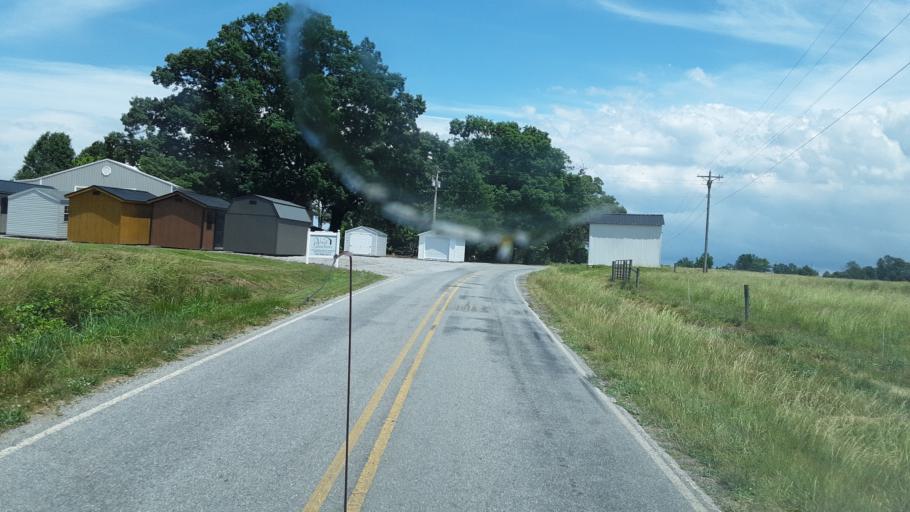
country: US
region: North Carolina
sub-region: Yadkin County
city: Yadkinville
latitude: 36.0683
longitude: -80.8153
